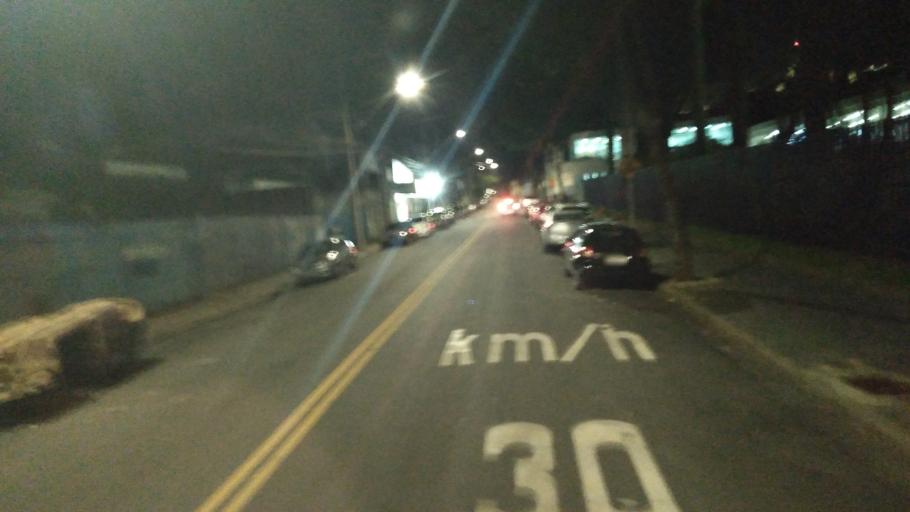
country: BR
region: Minas Gerais
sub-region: Belo Horizonte
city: Belo Horizonte
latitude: -19.9118
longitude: -43.9446
